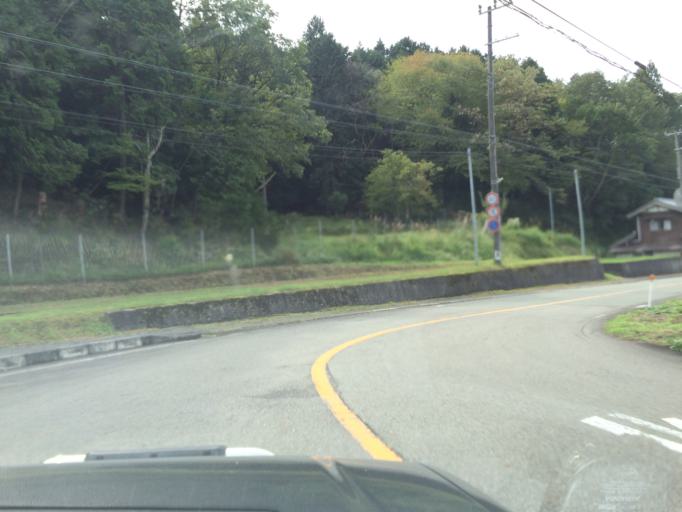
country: JP
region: Hyogo
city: Sasayama
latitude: 35.0711
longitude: 135.3128
